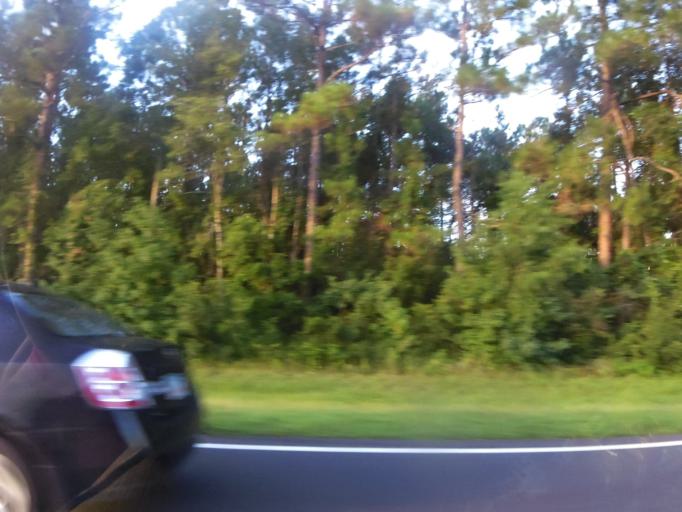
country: US
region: Georgia
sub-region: Camden County
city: Kingsland
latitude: 30.7972
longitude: -81.6739
